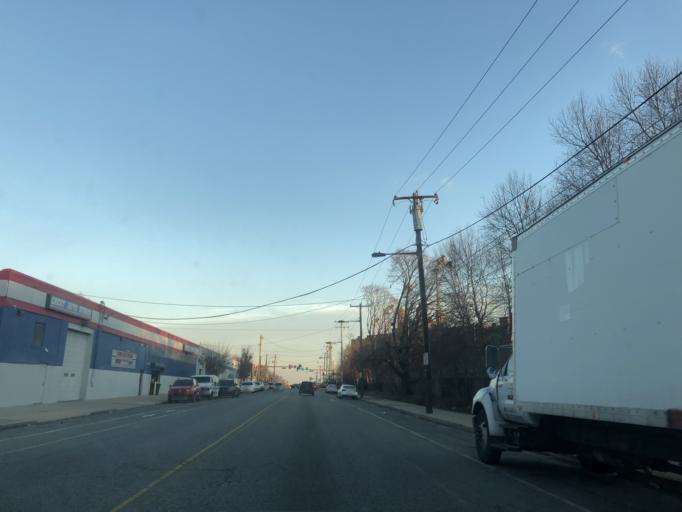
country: US
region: Pennsylvania
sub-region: Delaware County
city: Millbourne
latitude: 39.9826
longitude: -75.2412
